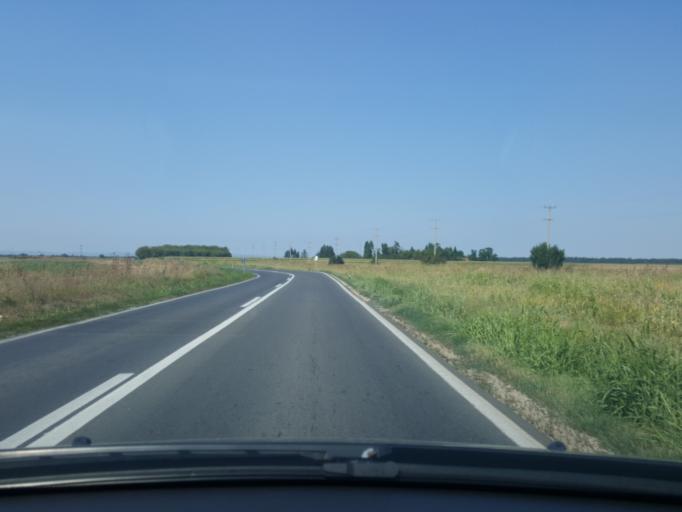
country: RS
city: Hrtkovci
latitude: 44.8507
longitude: 19.7705
